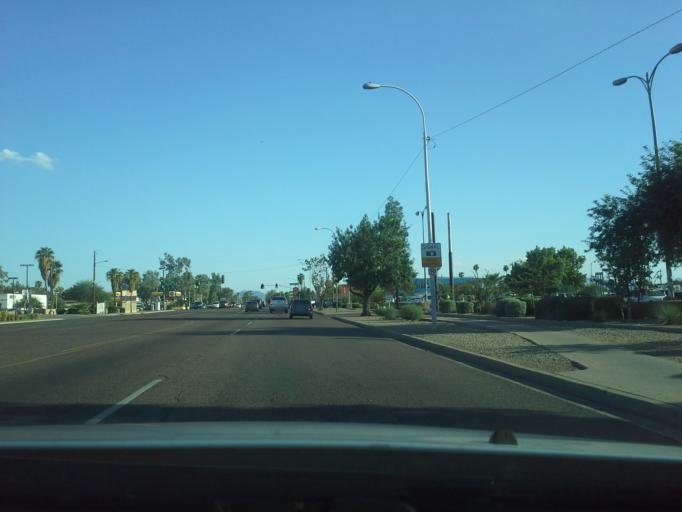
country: US
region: Arizona
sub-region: Maricopa County
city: Glendale
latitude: 33.5402
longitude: -112.1345
